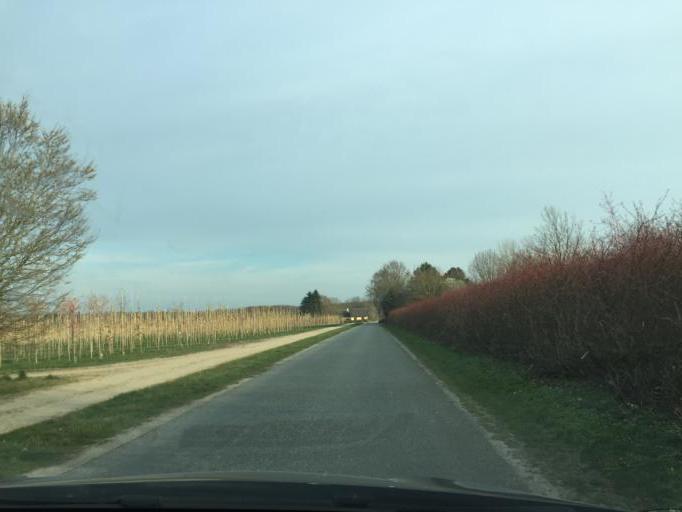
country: DK
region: South Denmark
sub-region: Kerteminde Kommune
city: Langeskov
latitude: 55.3301
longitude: 10.5803
